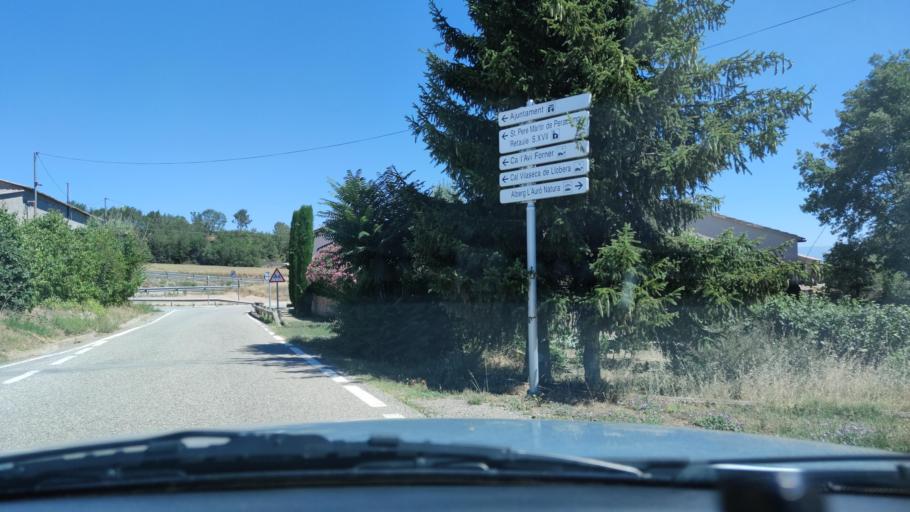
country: ES
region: Catalonia
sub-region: Provincia de Lleida
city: Solsona
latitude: 41.9211
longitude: 1.4615
